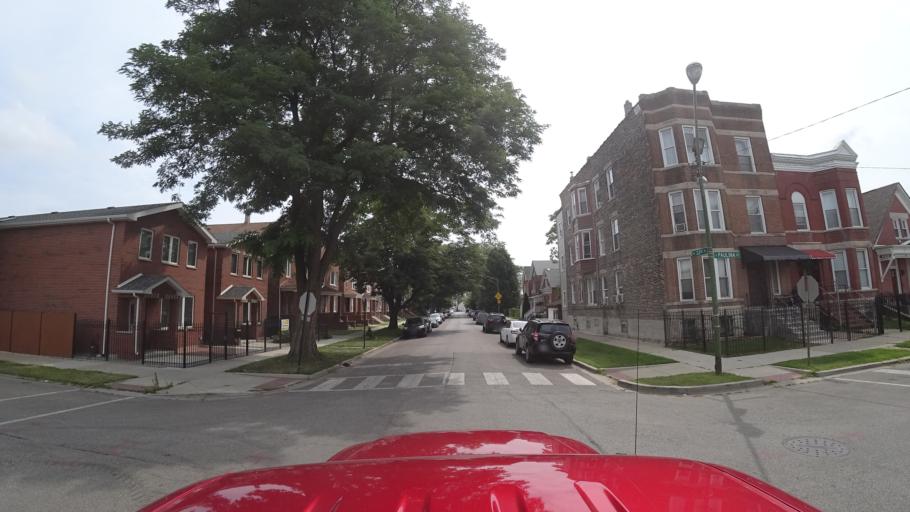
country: US
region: Illinois
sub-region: Cook County
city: Chicago
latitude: 41.8332
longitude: -87.6681
